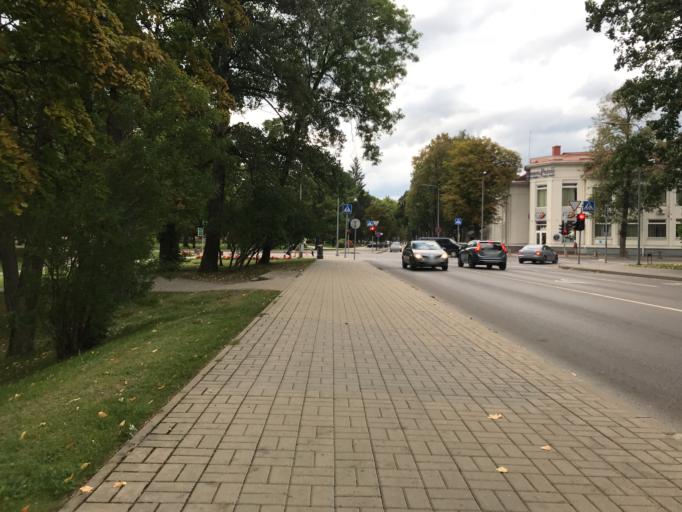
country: LT
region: Alytaus apskritis
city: Druskininkai
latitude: 54.0156
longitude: 23.9754
